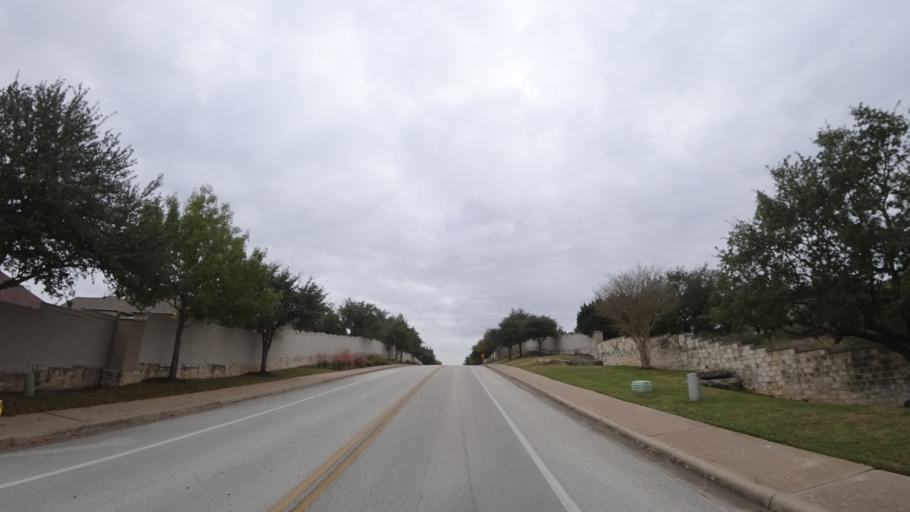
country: US
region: Texas
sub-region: Travis County
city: Bee Cave
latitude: 30.3179
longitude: -97.9168
